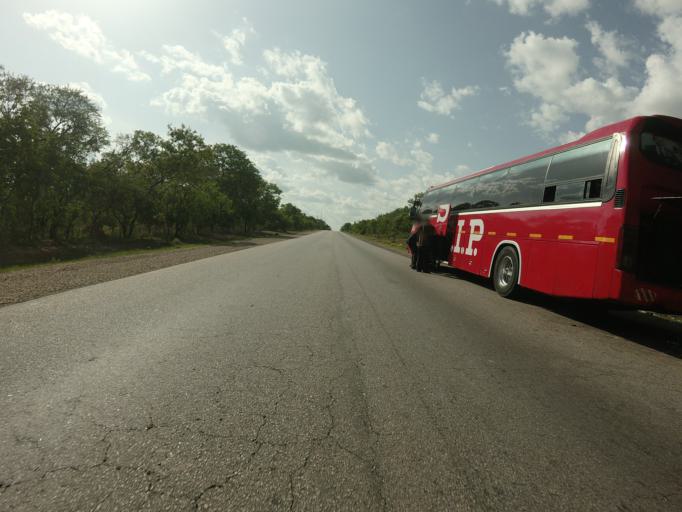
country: GH
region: Upper East
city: Bolgatanga
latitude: 10.5413
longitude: -0.8240
